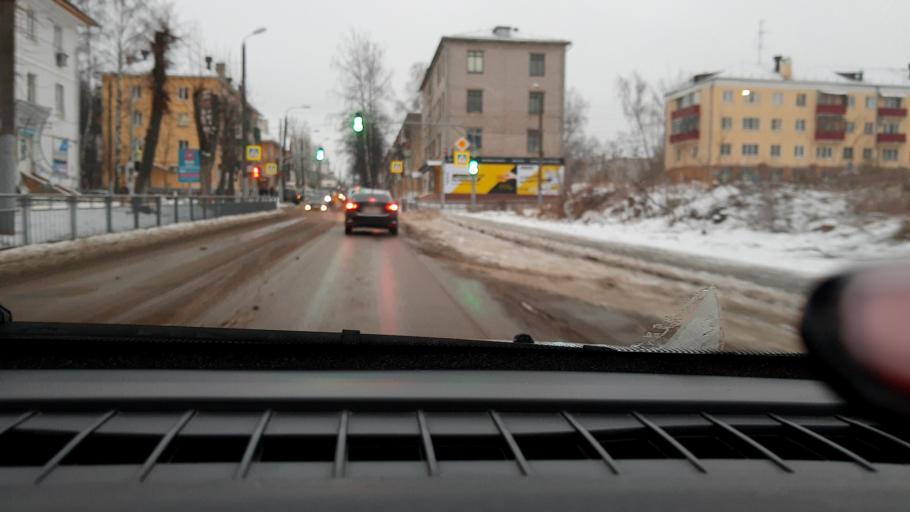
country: RU
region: Nizjnij Novgorod
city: Kstovo
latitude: 56.1516
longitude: 44.1978
